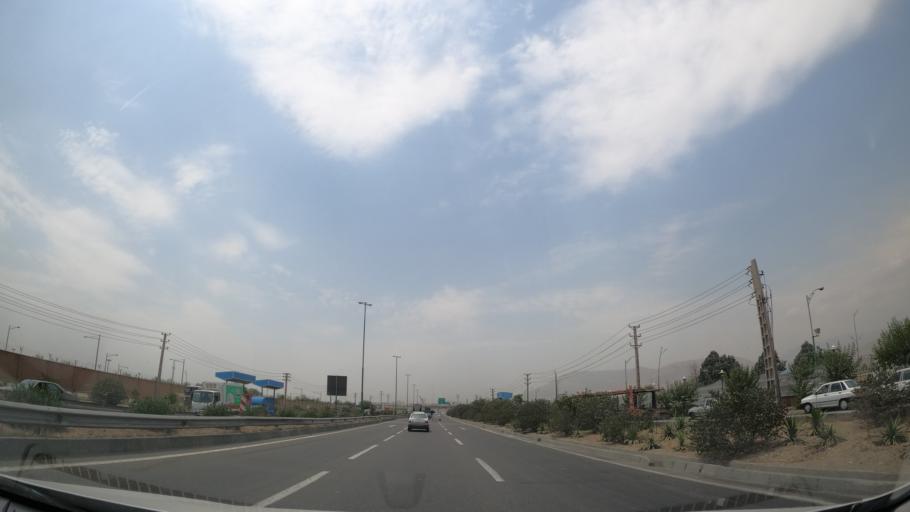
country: IR
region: Tehran
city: Shahr-e Qods
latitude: 35.7011
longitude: 51.1895
